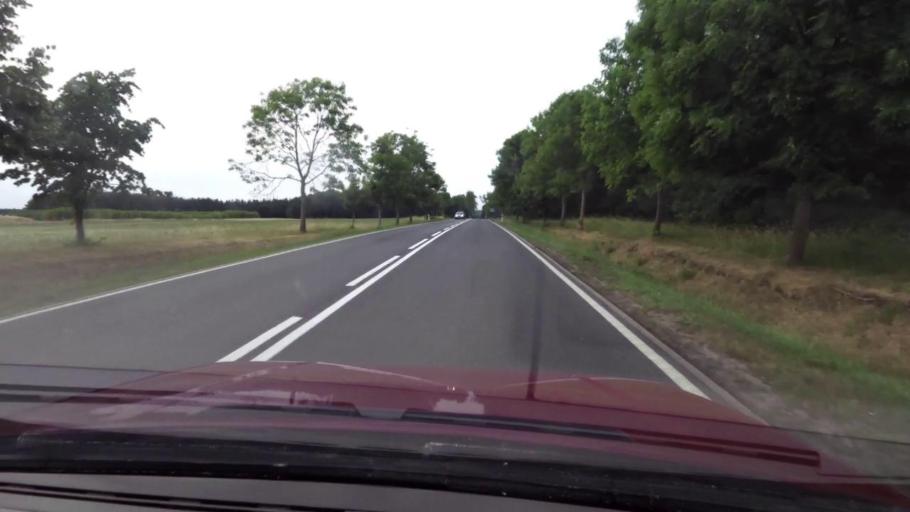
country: PL
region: Pomeranian Voivodeship
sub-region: Powiat bytowski
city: Trzebielino
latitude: 54.2677
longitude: 17.0993
